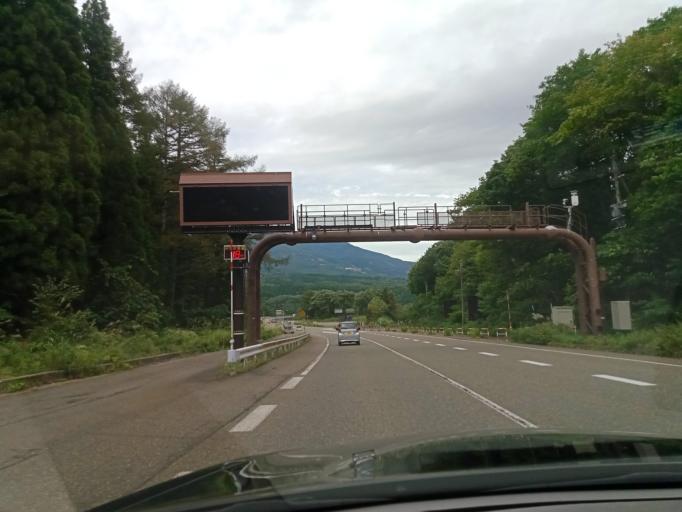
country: JP
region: Niigata
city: Arai
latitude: 36.8476
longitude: 138.1978
